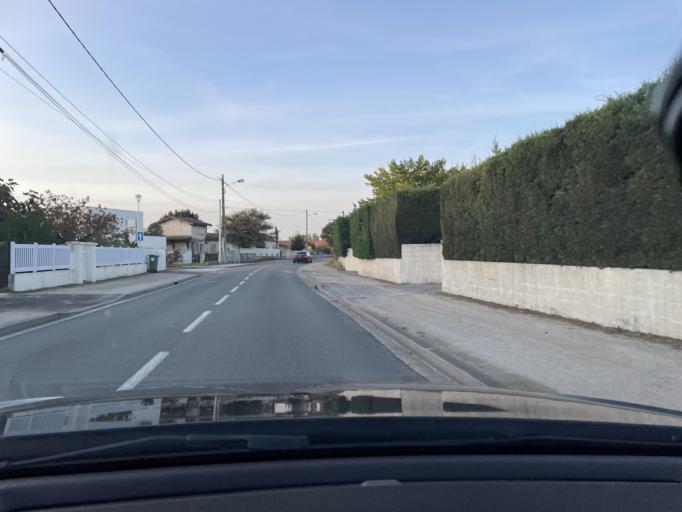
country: FR
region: Aquitaine
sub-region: Departement de la Gironde
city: Villenave-d'Ornon
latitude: 44.7772
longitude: -0.5390
